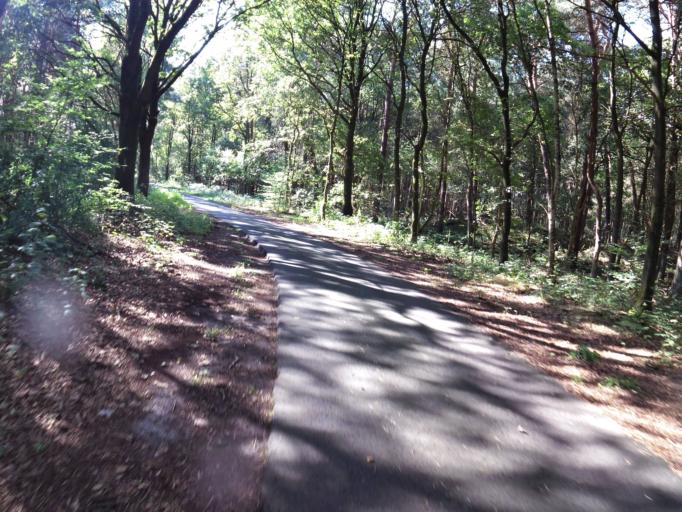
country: DE
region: Lower Saxony
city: Sandbostel
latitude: 53.3950
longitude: 9.1208
